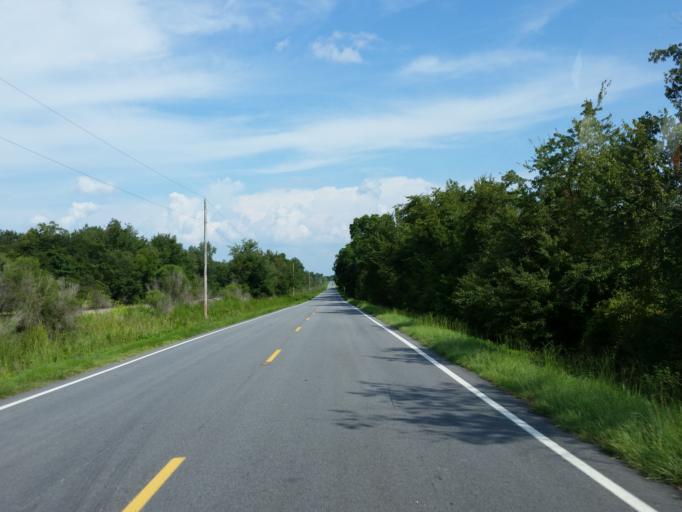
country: US
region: Georgia
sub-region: Turner County
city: Ashburn
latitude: 31.8146
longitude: -83.7239
